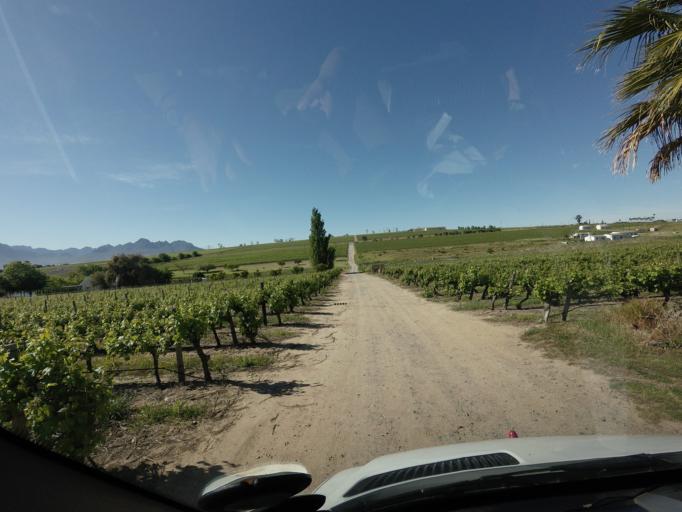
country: ZA
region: Western Cape
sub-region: Cape Winelands District Municipality
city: Stellenbosch
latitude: -33.9510
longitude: 18.7729
